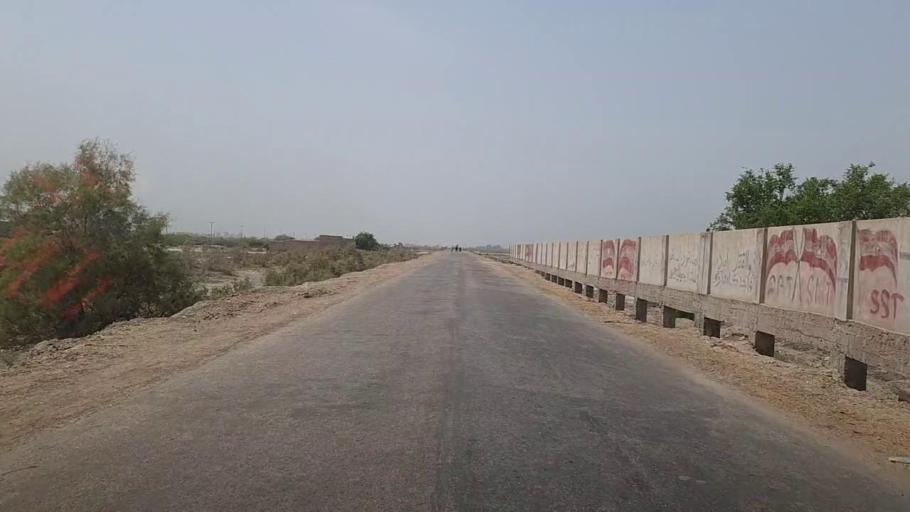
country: PK
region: Sindh
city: Radhan
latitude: 27.1611
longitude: 67.9428
